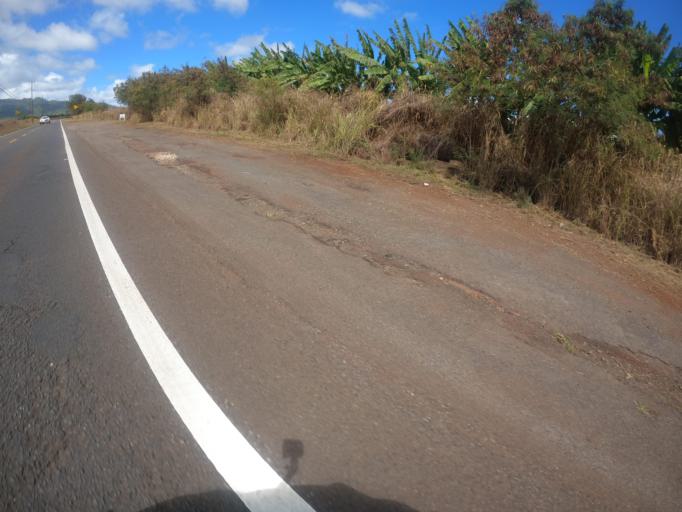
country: US
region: Hawaii
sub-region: Honolulu County
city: Village Park
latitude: 21.4247
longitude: -158.0531
